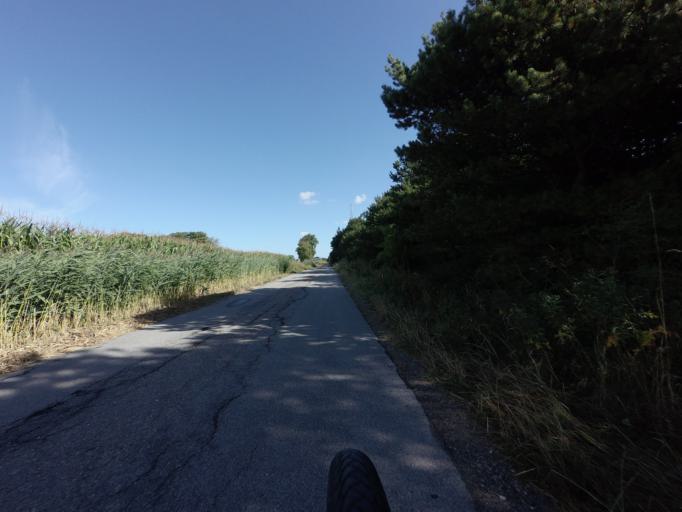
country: DK
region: North Denmark
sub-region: Hjorring Kommune
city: Vra
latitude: 57.4039
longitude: 9.9555
